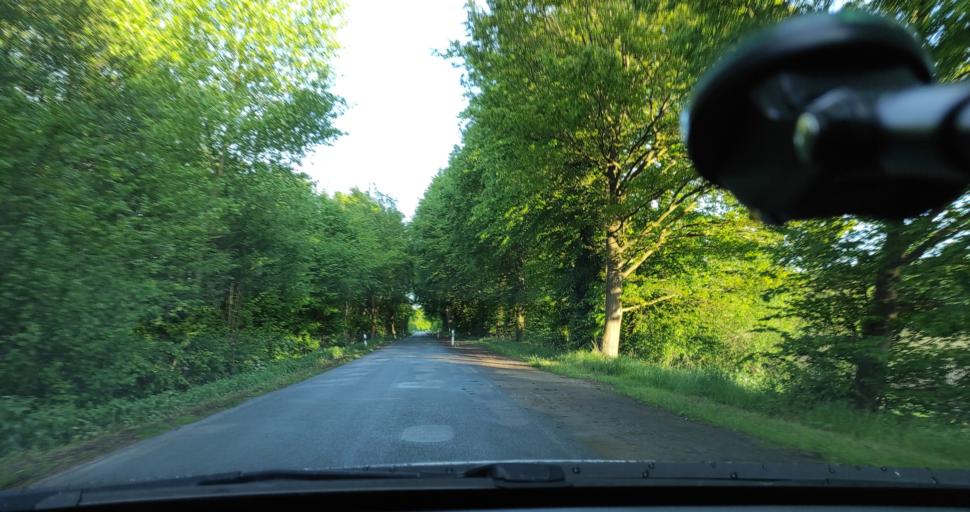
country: DE
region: North Rhine-Westphalia
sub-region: Regierungsbezirk Munster
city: Greven
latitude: 52.0835
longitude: 7.5708
